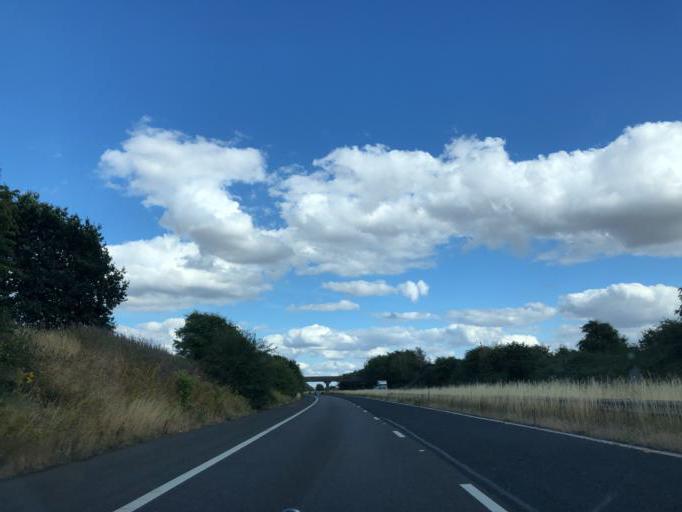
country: GB
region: England
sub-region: Northamptonshire
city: Daventry
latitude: 52.3286
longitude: -1.1684
